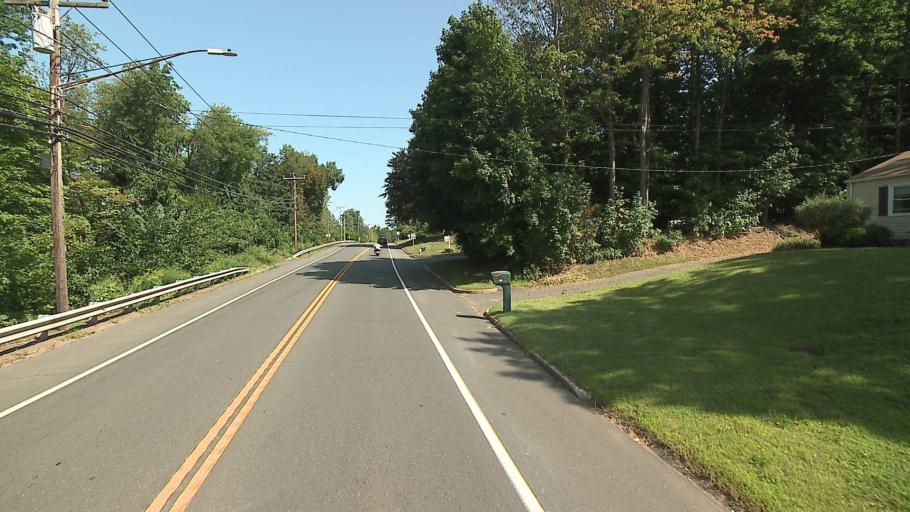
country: US
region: Connecticut
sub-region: Hartford County
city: Windsor Locks
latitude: 41.9247
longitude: -72.6062
